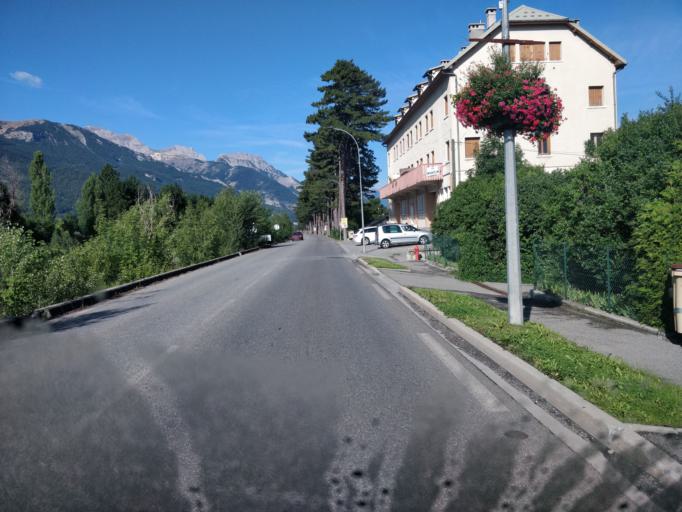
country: FR
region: Provence-Alpes-Cote d'Azur
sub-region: Departement des Alpes-de-Haute-Provence
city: Barcelonnette
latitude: 44.3863
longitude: 6.6411
